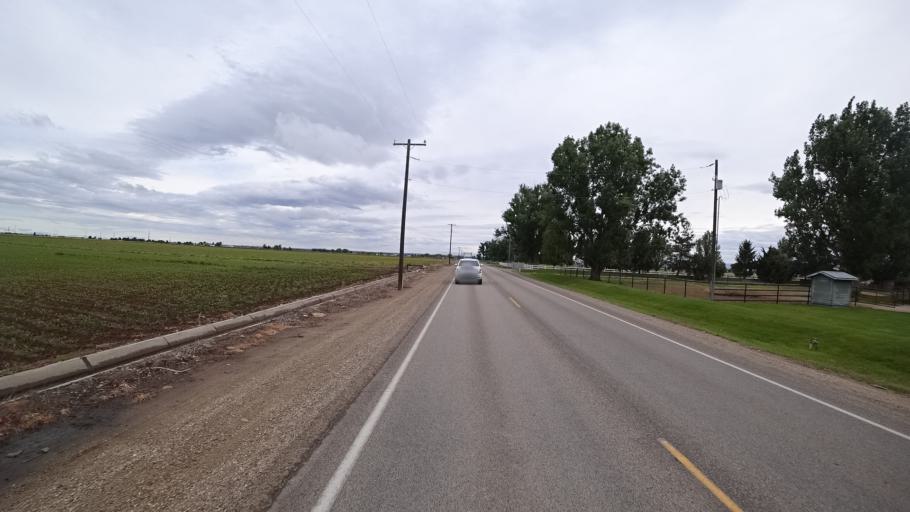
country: US
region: Idaho
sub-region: Ada County
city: Star
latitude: 43.6517
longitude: -116.4936
